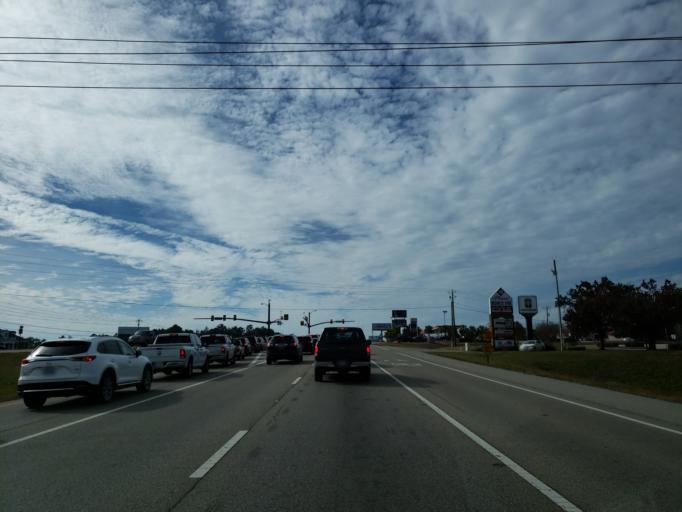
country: US
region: Mississippi
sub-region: Lamar County
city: West Hattiesburg
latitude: 31.3176
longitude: -89.4114
